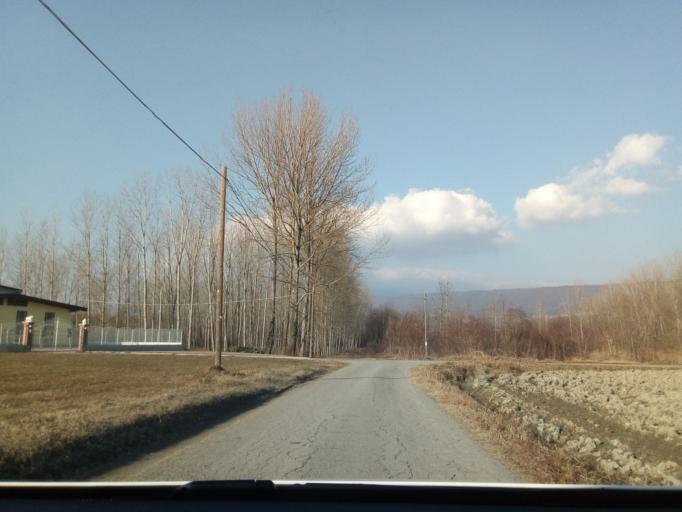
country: IT
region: Piedmont
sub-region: Provincia di Torino
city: Albiano d'Ivrea
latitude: 45.4506
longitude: 7.9404
